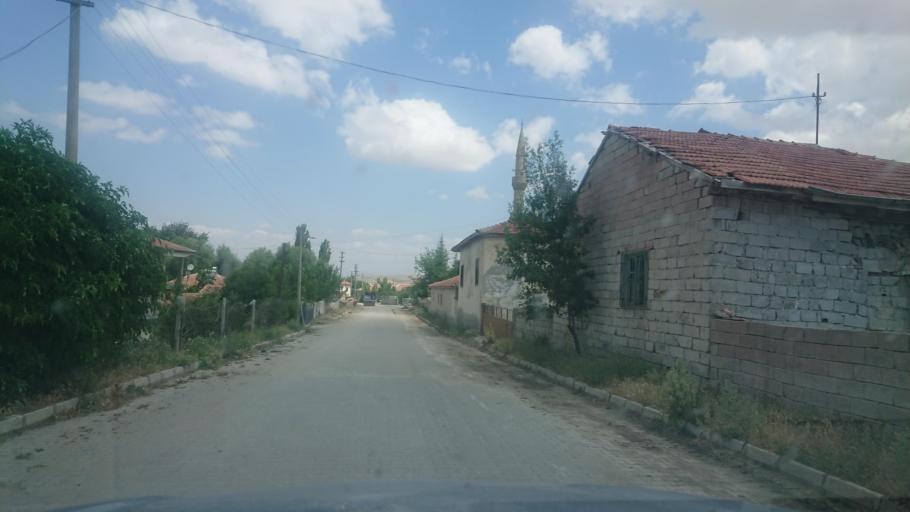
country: TR
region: Aksaray
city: Agacoren
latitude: 38.9299
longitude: 33.9574
